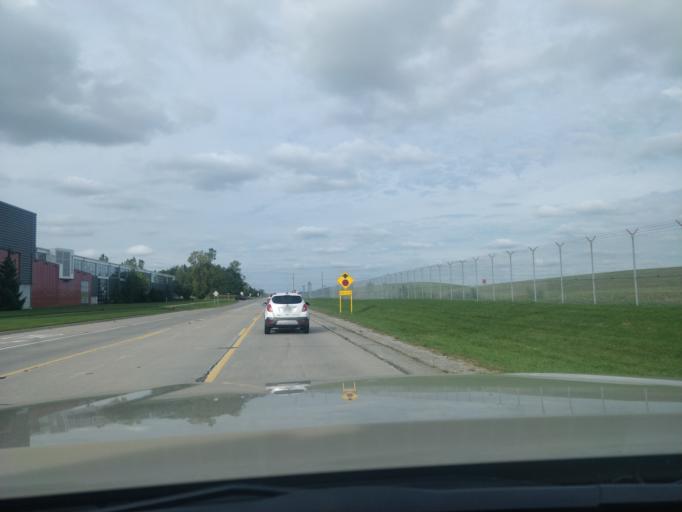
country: US
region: Michigan
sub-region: Wayne County
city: Romulus
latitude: 42.2066
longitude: -83.3872
